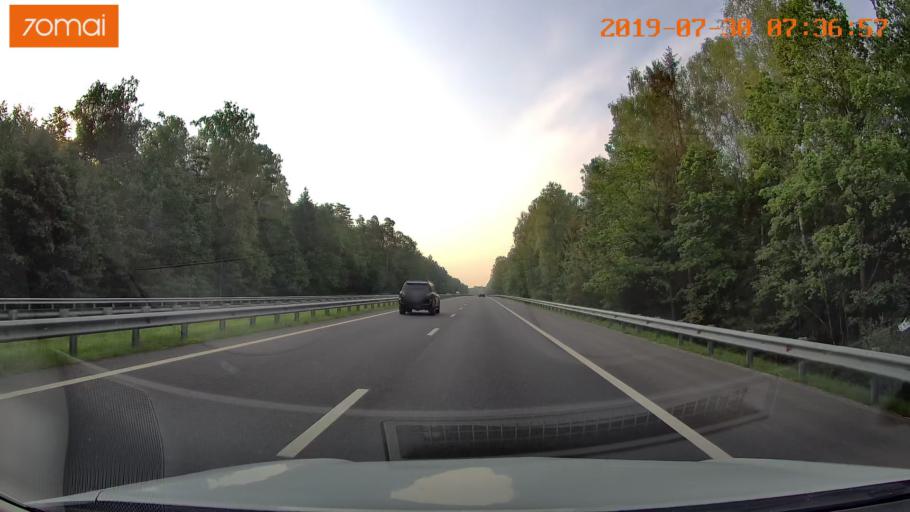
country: RU
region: Kaliningrad
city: Gvardeysk
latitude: 54.6599
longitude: 21.1360
